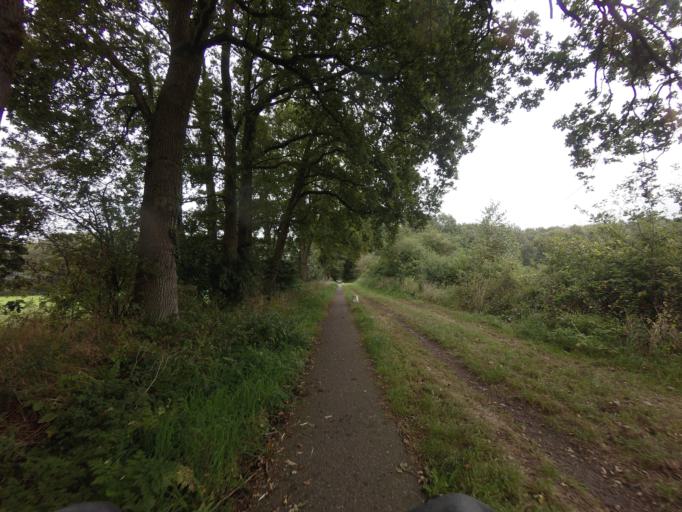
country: NL
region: Overijssel
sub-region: Gemeente Enschede
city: Enschede
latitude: 52.1853
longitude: 6.9410
